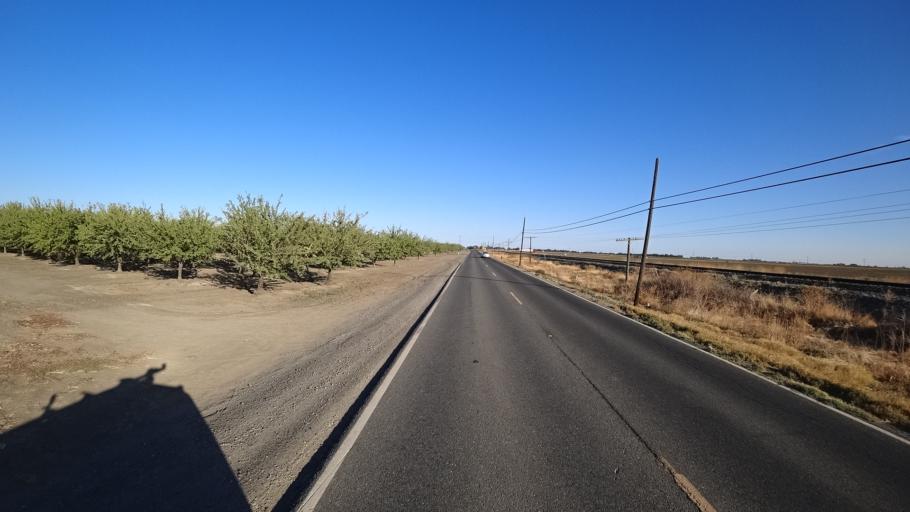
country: US
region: California
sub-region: Yolo County
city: Davis
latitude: 38.5865
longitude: -121.7514
